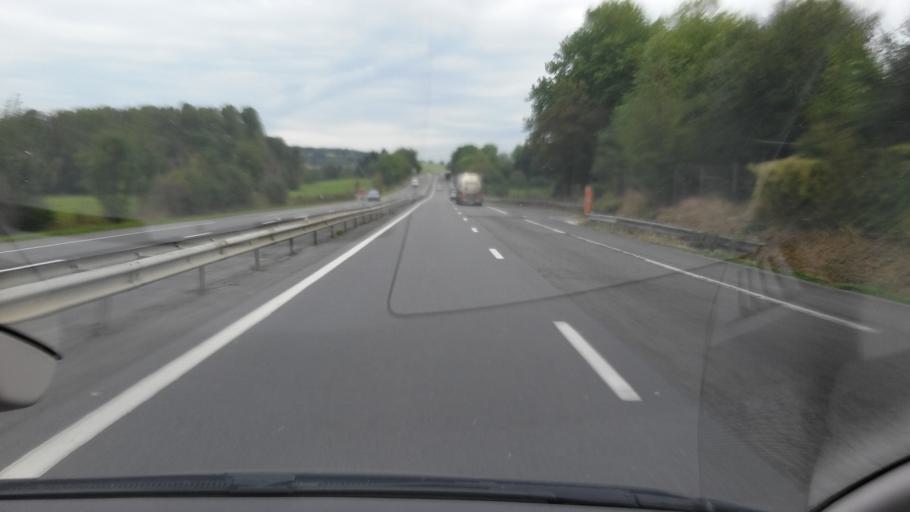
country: FR
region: Champagne-Ardenne
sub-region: Departement des Ardennes
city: La Francheville
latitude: 49.6841
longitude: 4.6699
